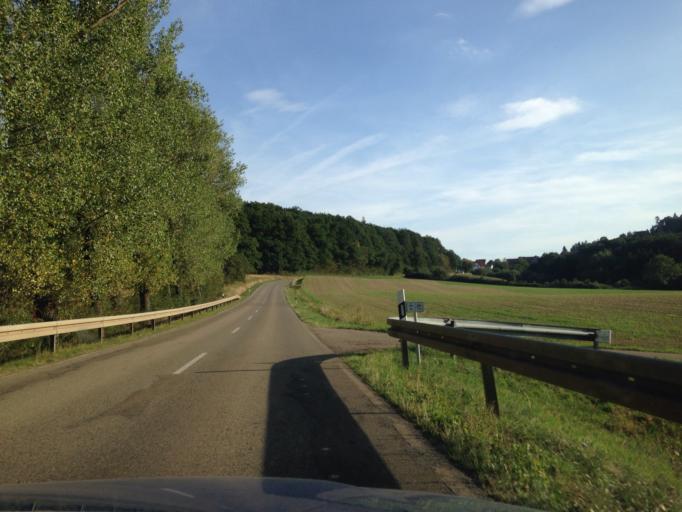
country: DE
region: Bavaria
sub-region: Regierungsbezirk Mittelfranken
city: Thalmassing
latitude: 49.1238
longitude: 11.2124
